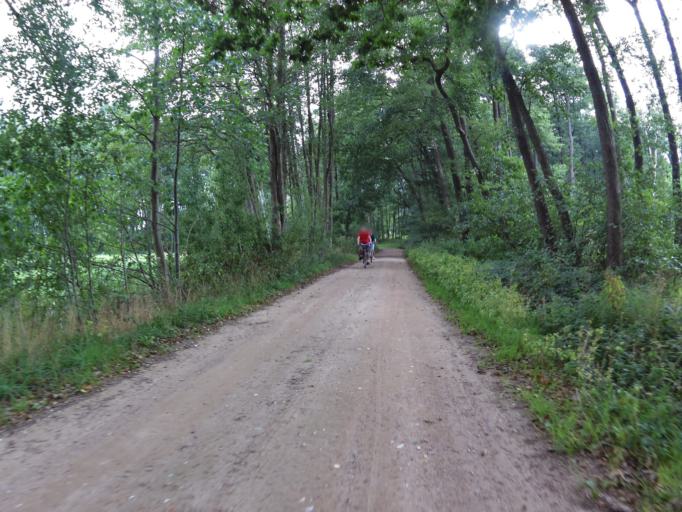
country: DE
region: Mecklenburg-Vorpommern
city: Seebad Heringsdorf
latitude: 53.9352
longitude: 14.1471
